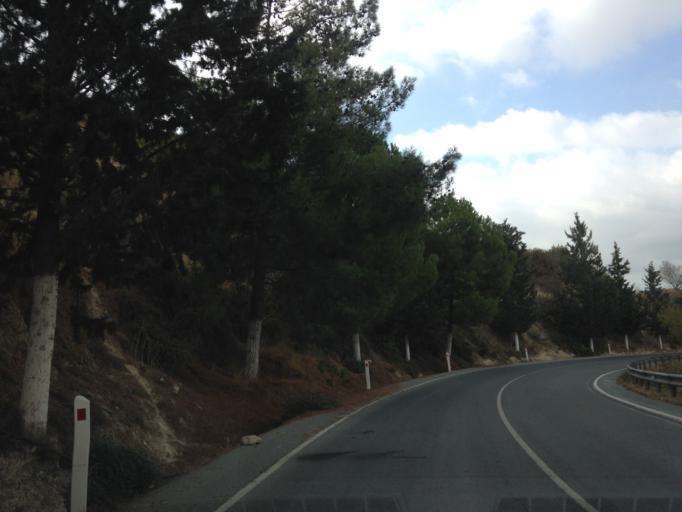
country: CY
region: Limassol
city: Pachna
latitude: 34.7818
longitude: 32.7966
